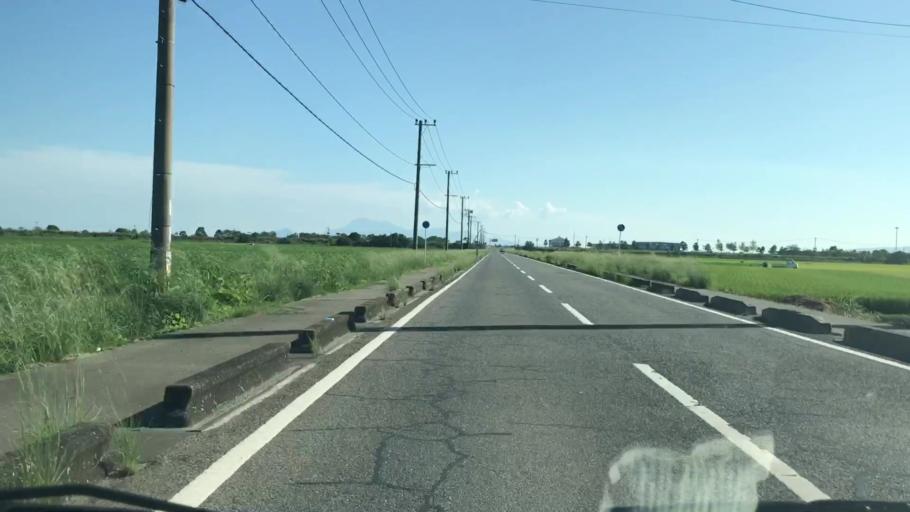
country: JP
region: Saga Prefecture
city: Okawa
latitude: 33.1582
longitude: 130.3085
